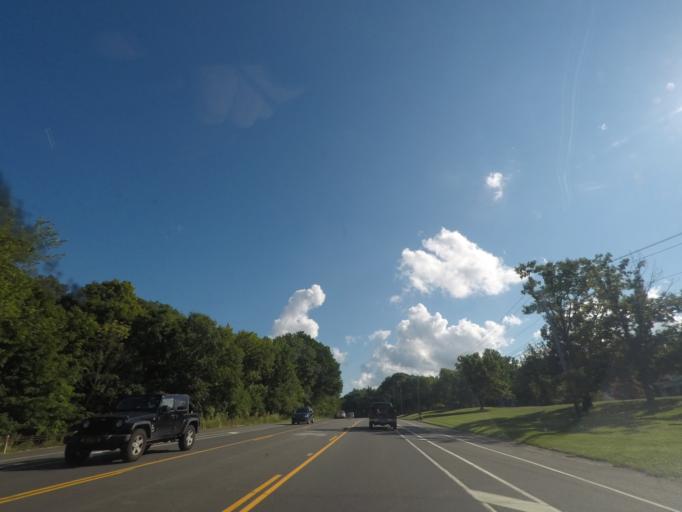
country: US
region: New York
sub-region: Albany County
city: Menands
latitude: 42.6961
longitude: -73.7399
